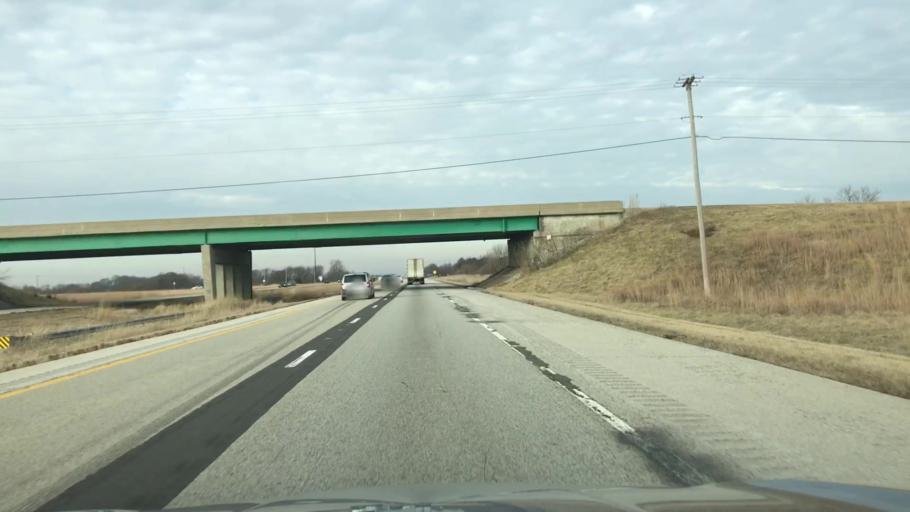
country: US
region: Illinois
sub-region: Sangamon County
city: Divernon
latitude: 39.5672
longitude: -89.6460
